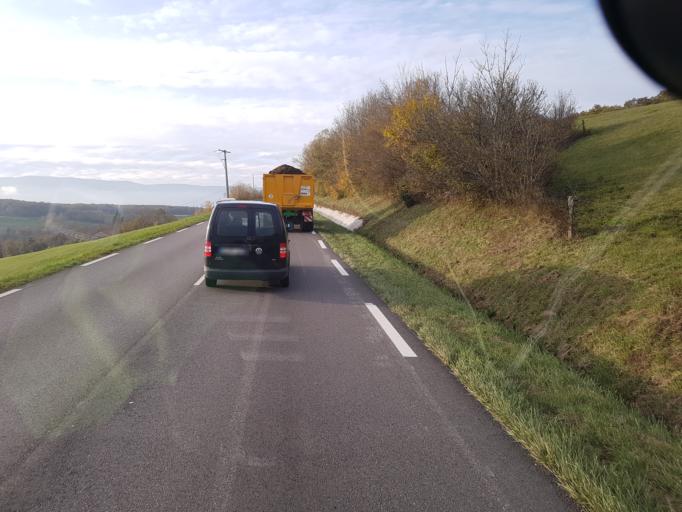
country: FR
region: Rhone-Alpes
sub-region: Departement de la Haute-Savoie
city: Frangy
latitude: 46.0540
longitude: 5.8757
